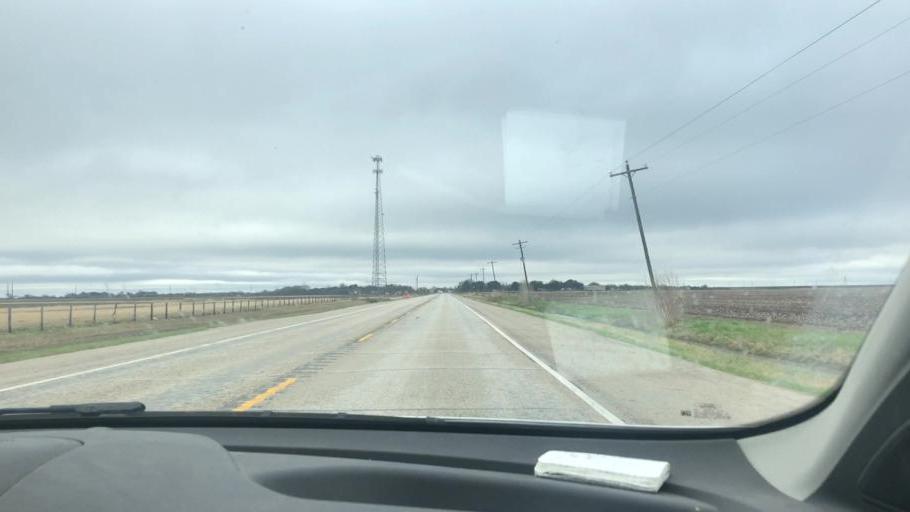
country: US
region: Texas
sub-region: Wharton County
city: Boling
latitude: 29.2332
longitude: -96.0375
